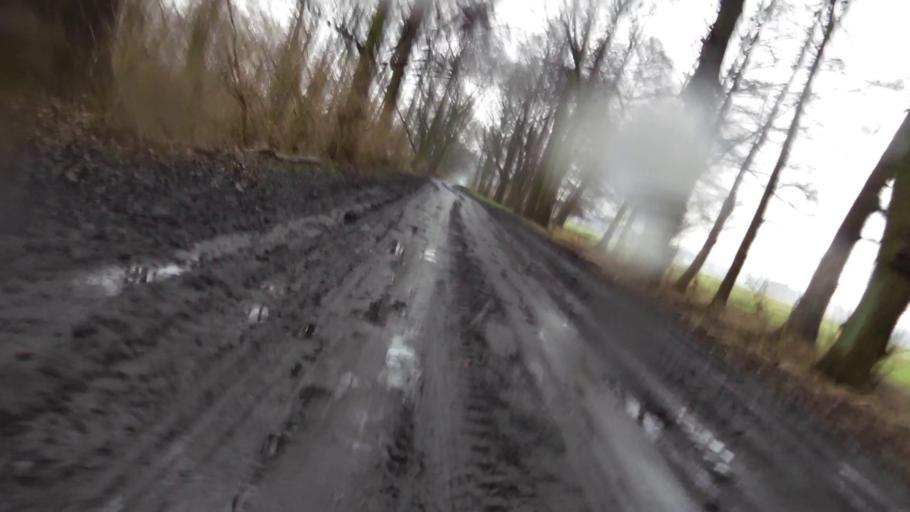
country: PL
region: West Pomeranian Voivodeship
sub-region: Powiat goleniowski
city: Goleniow
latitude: 53.4386
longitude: 14.7222
